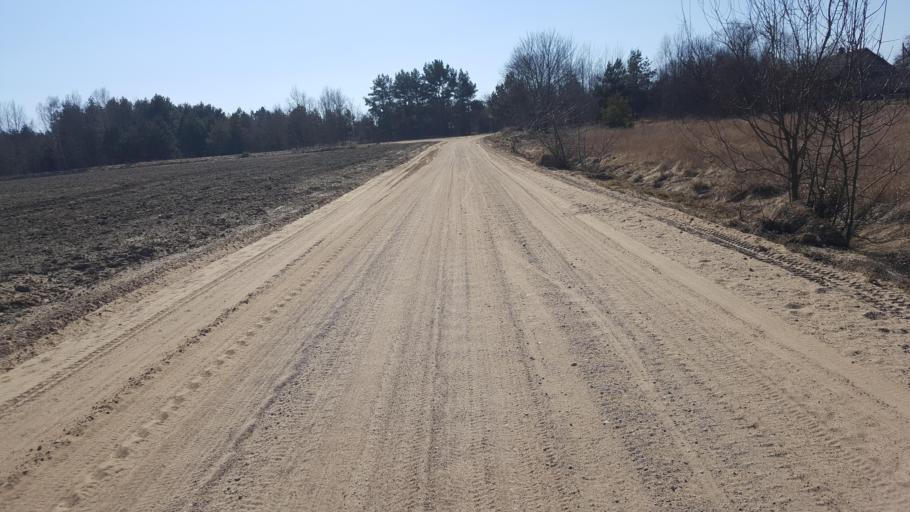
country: BY
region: Brest
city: Kamyanyets
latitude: 52.3535
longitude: 23.7569
